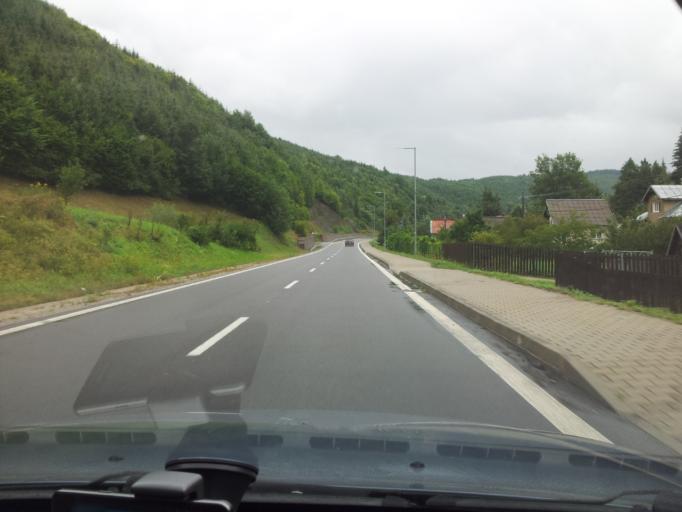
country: SK
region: Banskobystricky
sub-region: Okres Banska Bystrica
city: Brezno
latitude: 48.8235
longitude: 19.5619
